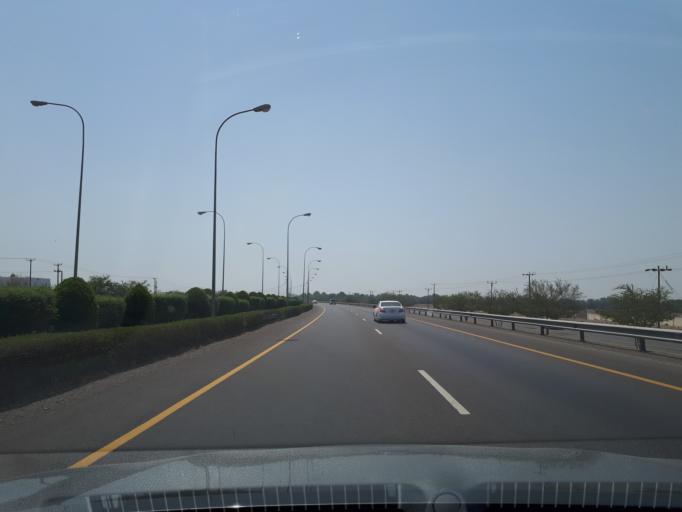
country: OM
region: Al Batinah
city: Al Sohar
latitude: 24.4101
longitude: 56.6453
